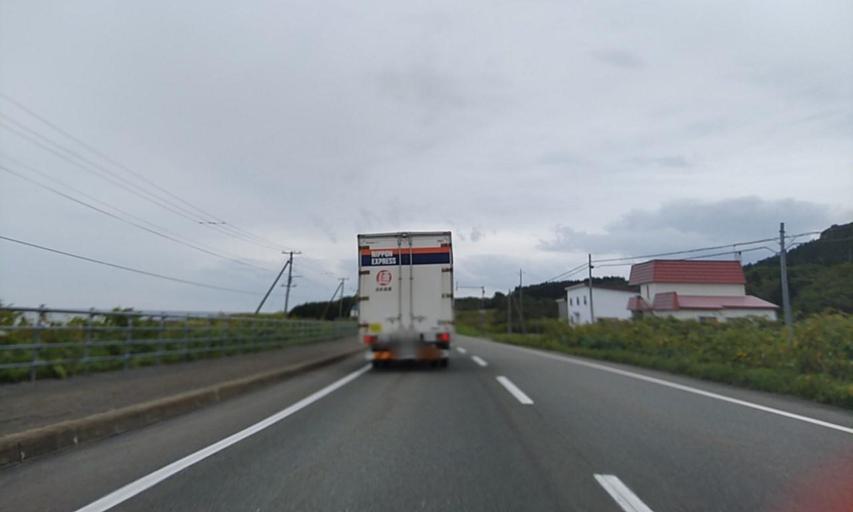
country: JP
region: Hokkaido
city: Nayoro
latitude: 45.0288
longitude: 142.5222
